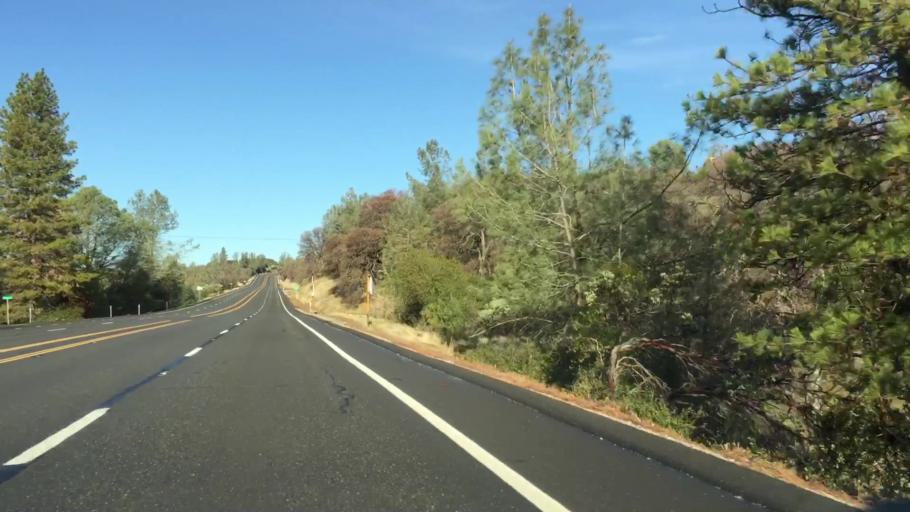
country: US
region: California
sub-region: Butte County
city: Paradise
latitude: 39.6756
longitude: -121.5324
